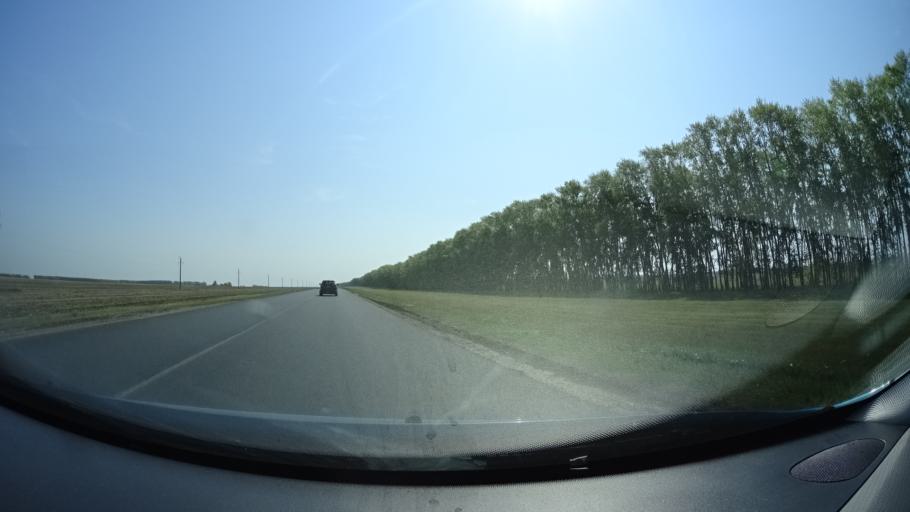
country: RU
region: Bashkortostan
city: Karmaskaly
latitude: 54.4148
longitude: 56.0570
